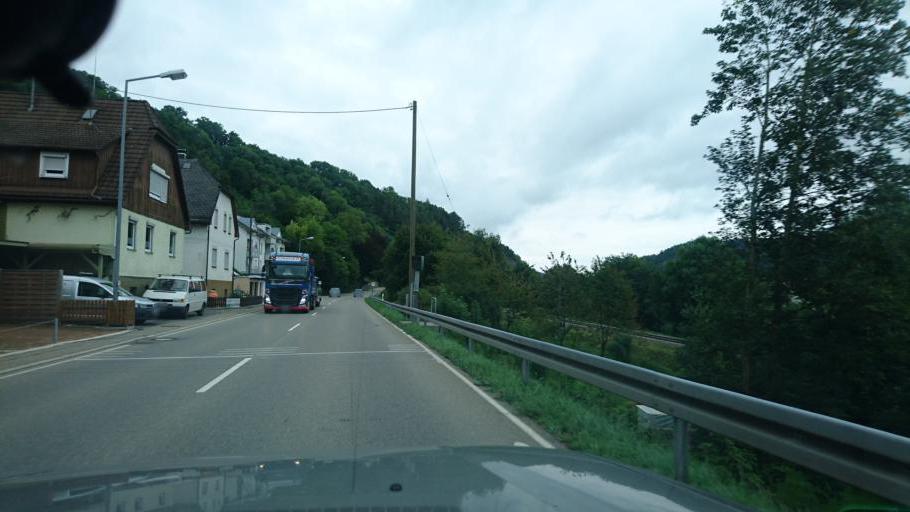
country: DE
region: Baden-Wuerttemberg
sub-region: Freiburg Region
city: Sulz am Neckar
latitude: 48.3609
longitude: 8.6236
